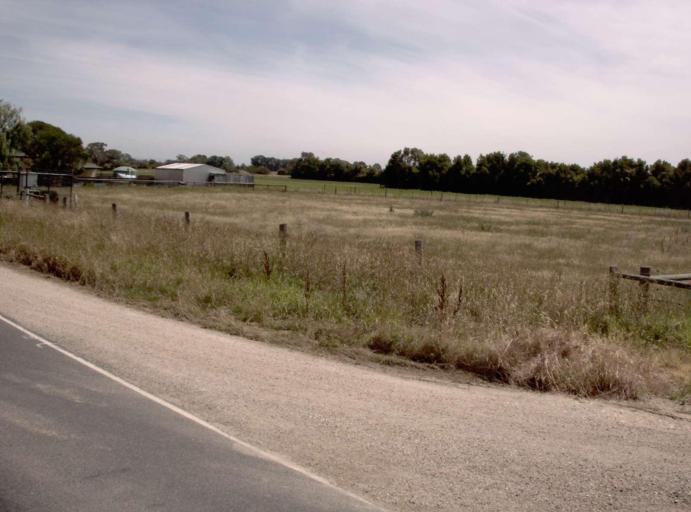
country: AU
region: Victoria
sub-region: Wellington
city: Heyfield
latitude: -38.0454
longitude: 146.8761
